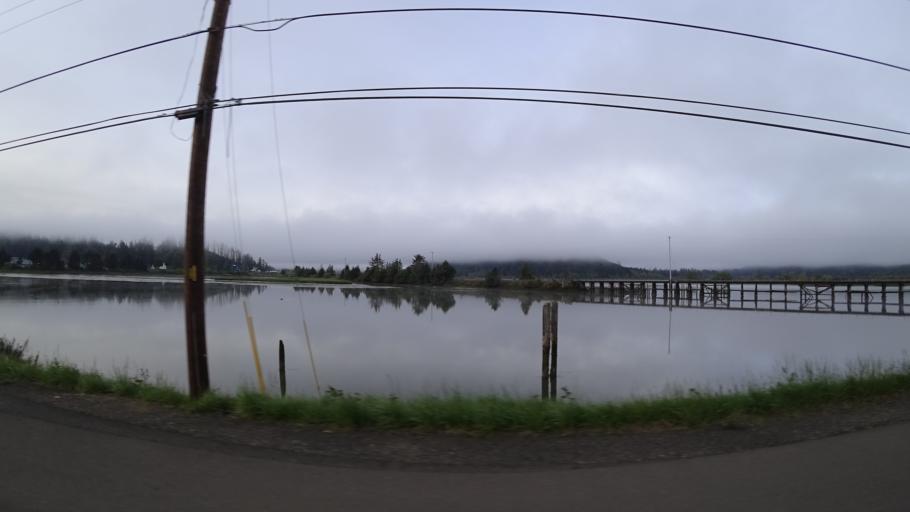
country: US
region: Oregon
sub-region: Douglas County
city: Reedsport
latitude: 43.7207
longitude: -124.1058
